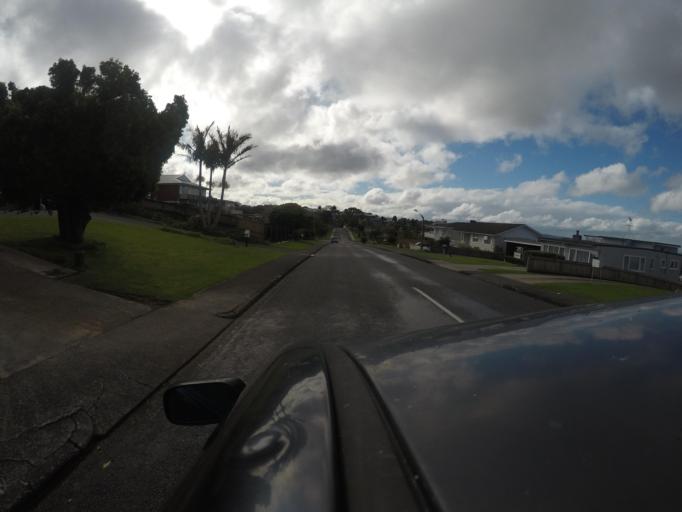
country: NZ
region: Auckland
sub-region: Auckland
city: Rosebank
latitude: -36.8905
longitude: 174.6460
